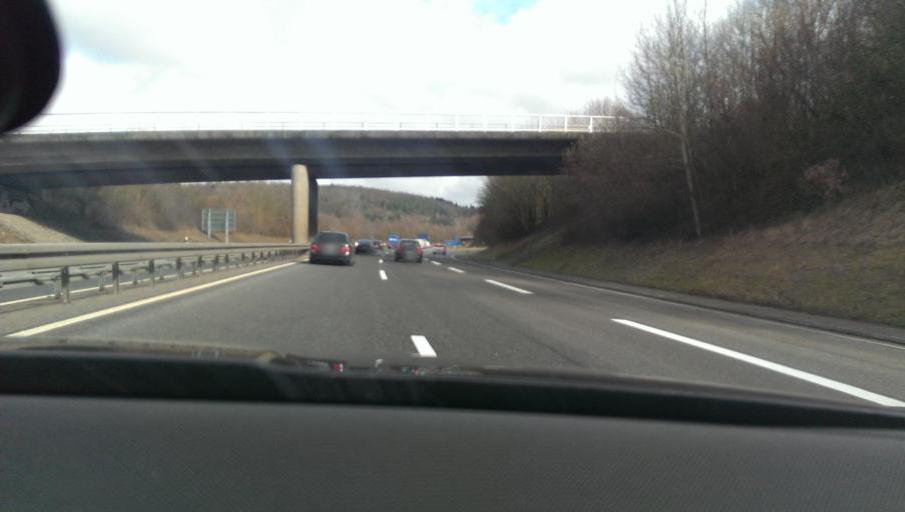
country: DE
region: Hesse
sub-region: Regierungsbezirk Darmstadt
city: Steinau an der Strasse
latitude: 50.3152
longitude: 9.4301
